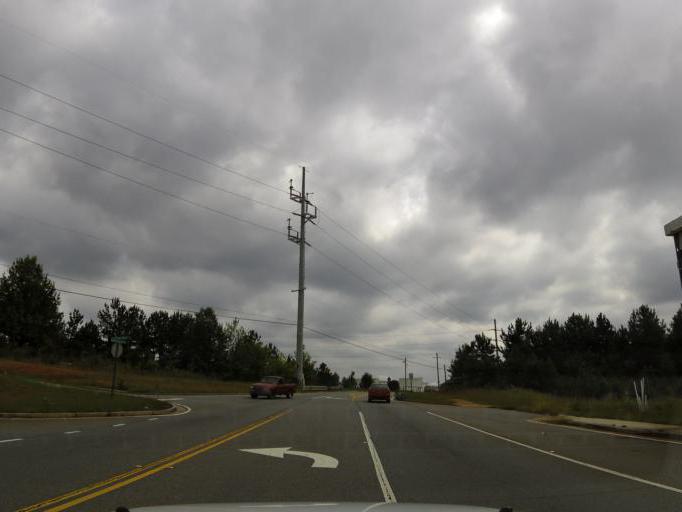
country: US
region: Georgia
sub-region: Cobb County
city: Powder Springs
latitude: 33.8657
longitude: -84.6332
